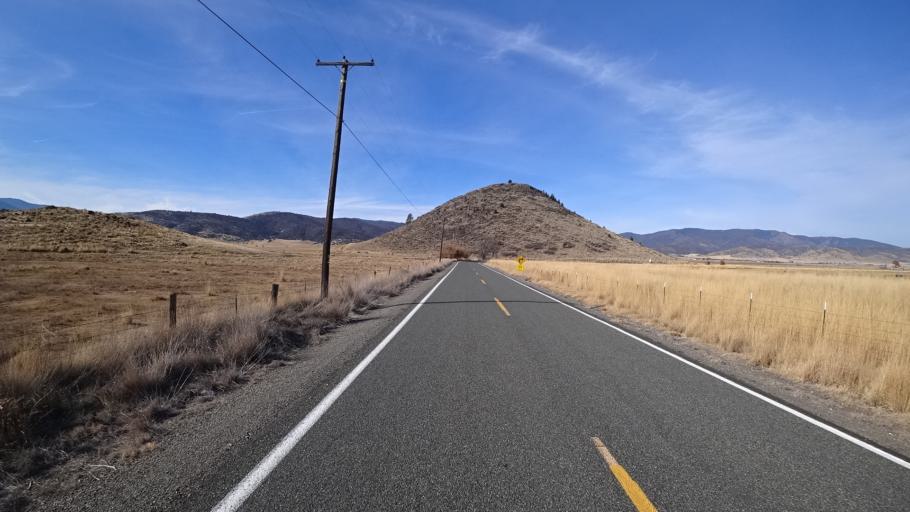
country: US
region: California
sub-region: Siskiyou County
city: Weed
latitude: 41.5342
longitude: -122.5165
